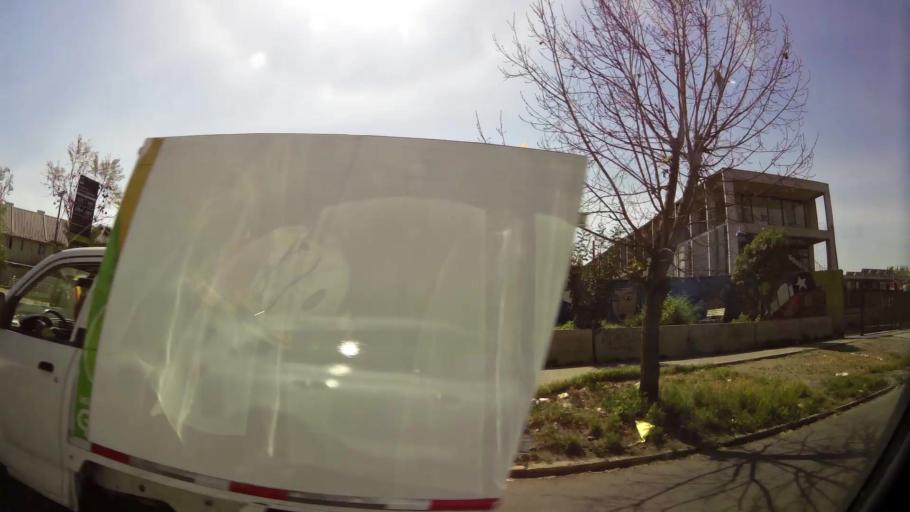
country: CL
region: Santiago Metropolitan
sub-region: Provincia de Maipo
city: San Bernardo
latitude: -33.5253
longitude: -70.7033
